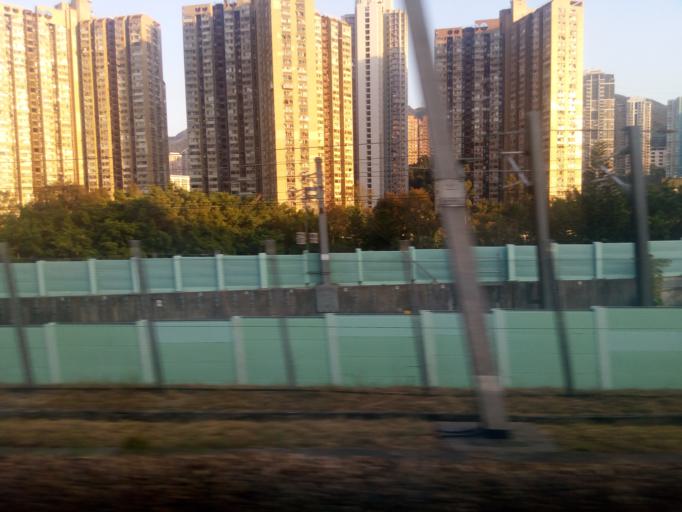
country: HK
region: Wong Tai Sin
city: Wong Tai Sin
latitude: 22.3657
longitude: 114.1713
